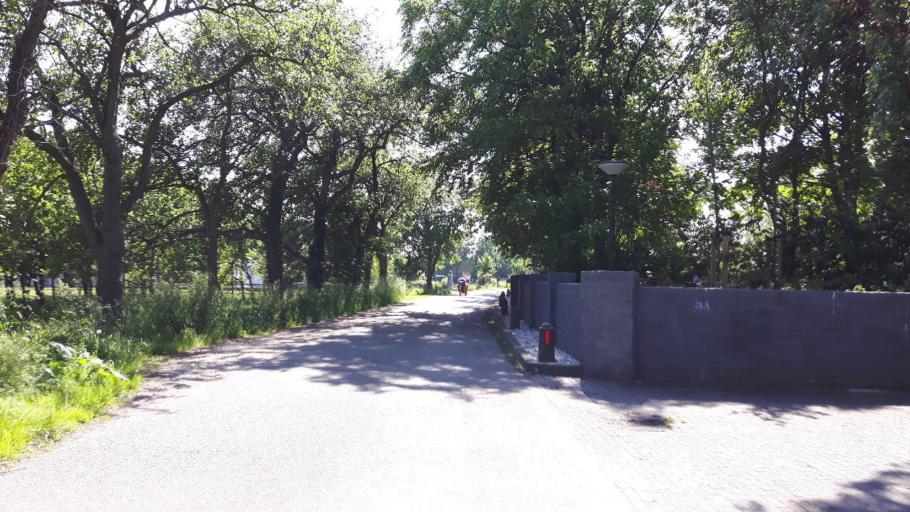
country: NL
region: Utrecht
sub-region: Stichtse Vecht
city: Vreeland
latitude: 52.2424
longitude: 5.0454
